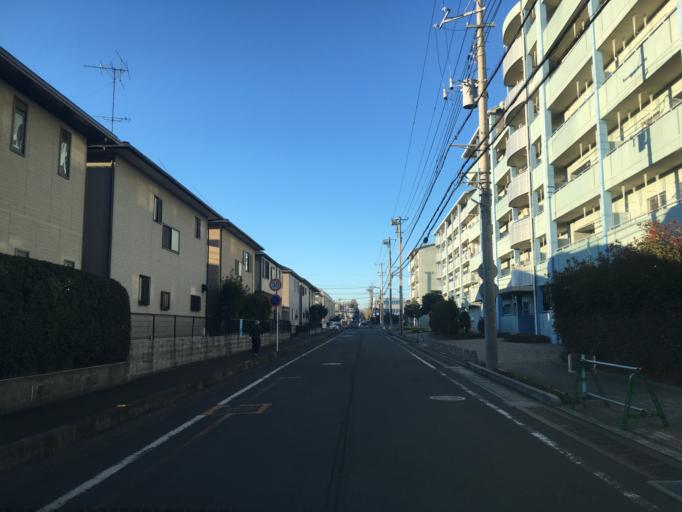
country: JP
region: Saitama
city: Sayama
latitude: 35.8251
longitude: 139.3981
